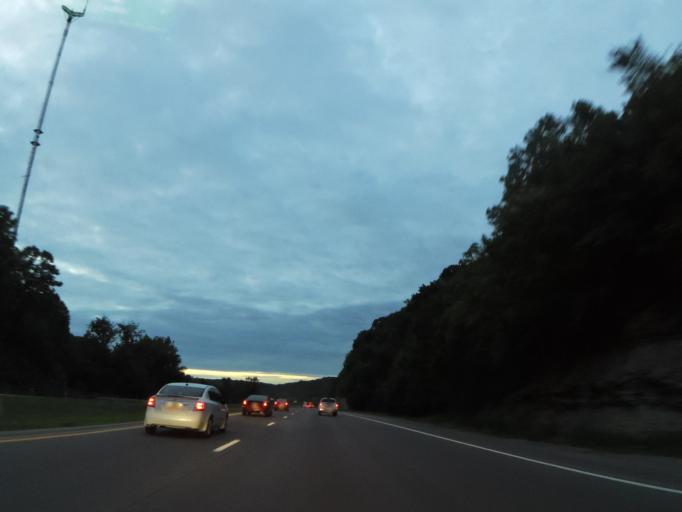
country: US
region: Tennessee
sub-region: Davidson County
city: Goodlettsville
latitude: 36.2655
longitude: -86.7910
